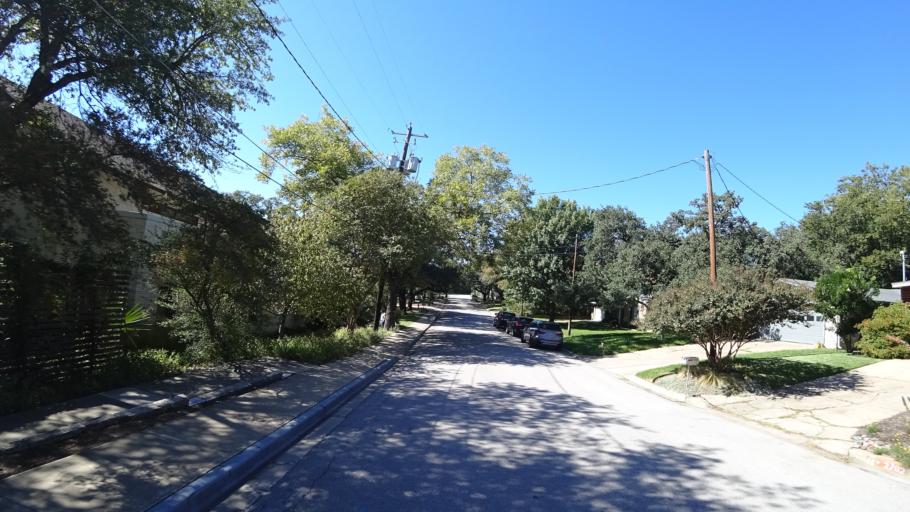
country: US
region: Texas
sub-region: Travis County
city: West Lake Hills
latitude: 30.3089
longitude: -97.7635
